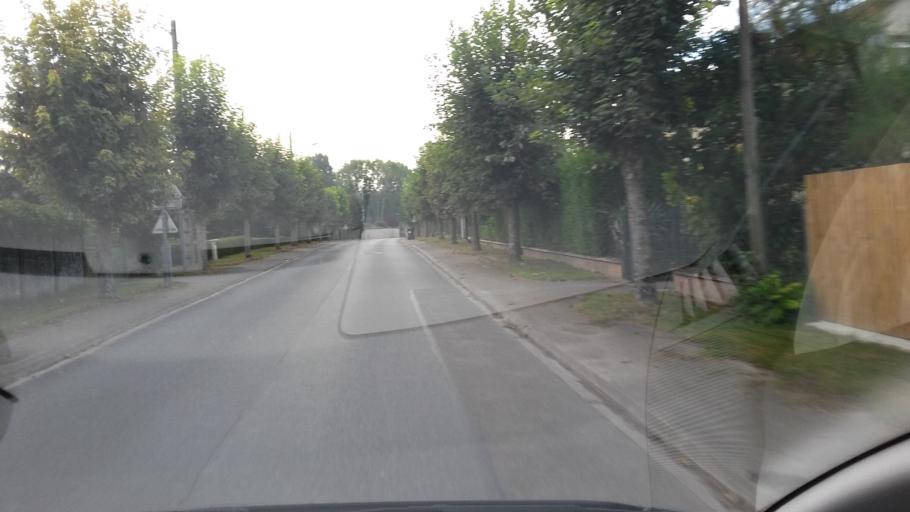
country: FR
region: Champagne-Ardenne
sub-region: Departement de la Marne
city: Connantre
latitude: 48.7309
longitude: 3.9234
